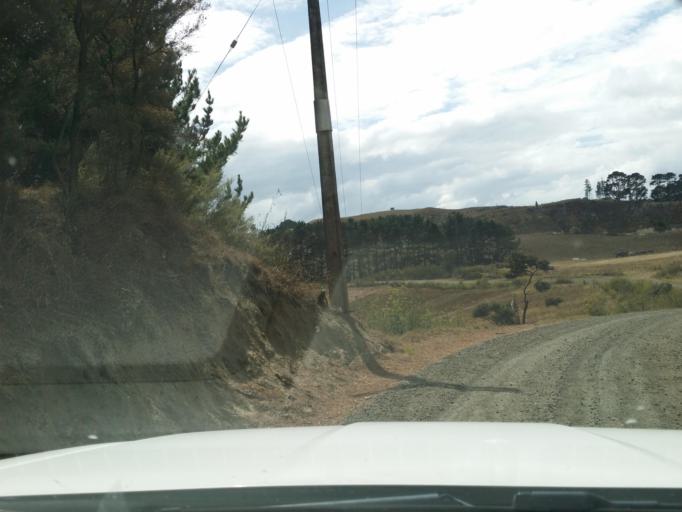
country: NZ
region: Auckland
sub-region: Auckland
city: Wellsford
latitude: -36.3332
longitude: 174.1549
